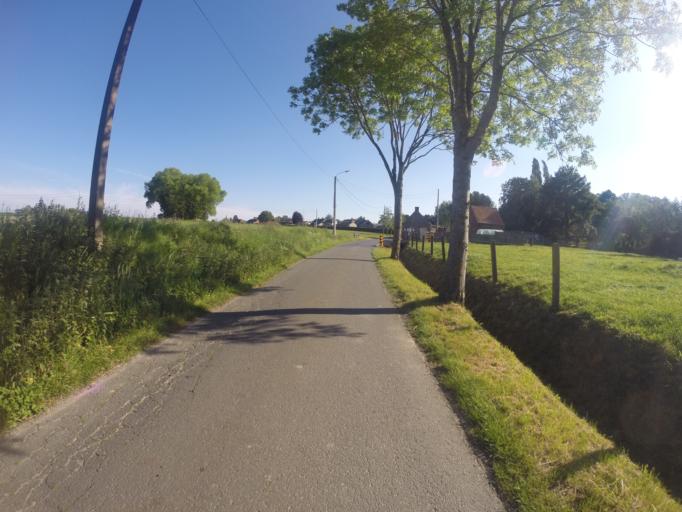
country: BE
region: Flanders
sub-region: Provincie West-Vlaanderen
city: Dentergem
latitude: 51.0034
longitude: 3.4208
